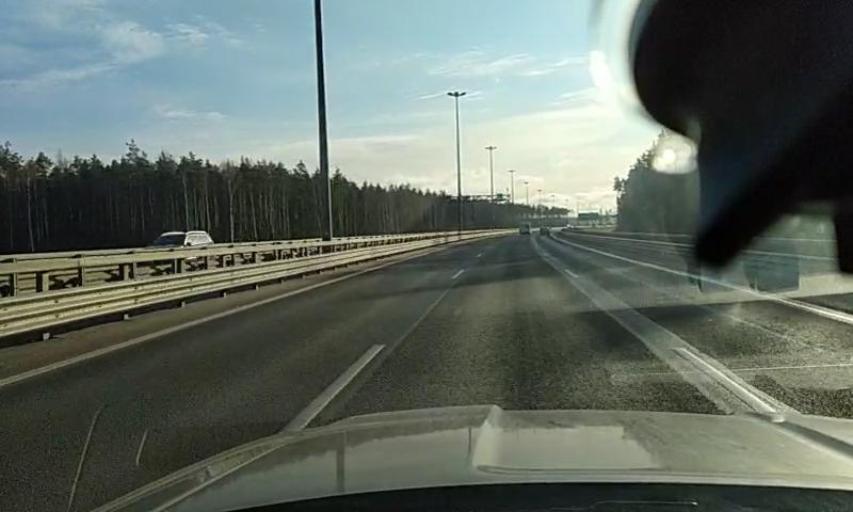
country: RU
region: St.-Petersburg
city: Pesochnyy
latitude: 60.0761
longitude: 30.1285
